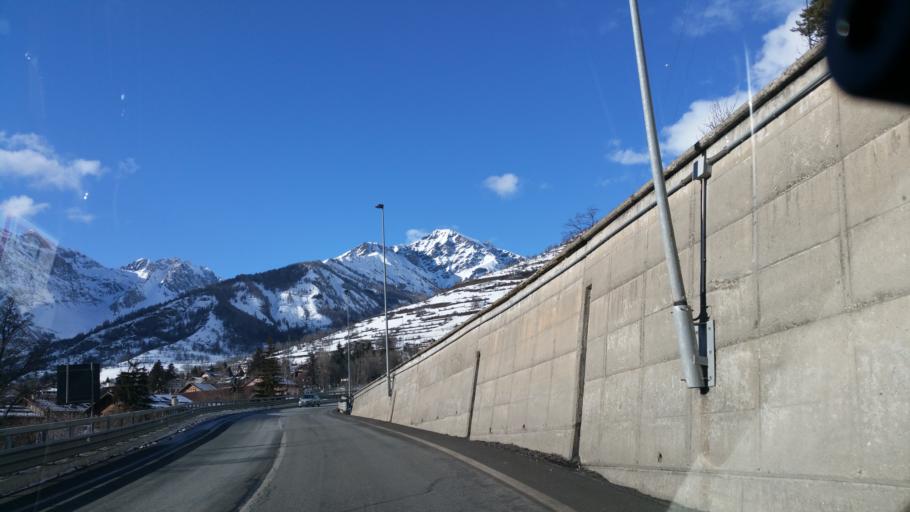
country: IT
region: Piedmont
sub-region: Provincia di Torino
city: Bardonecchia
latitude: 45.0776
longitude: 6.7121
